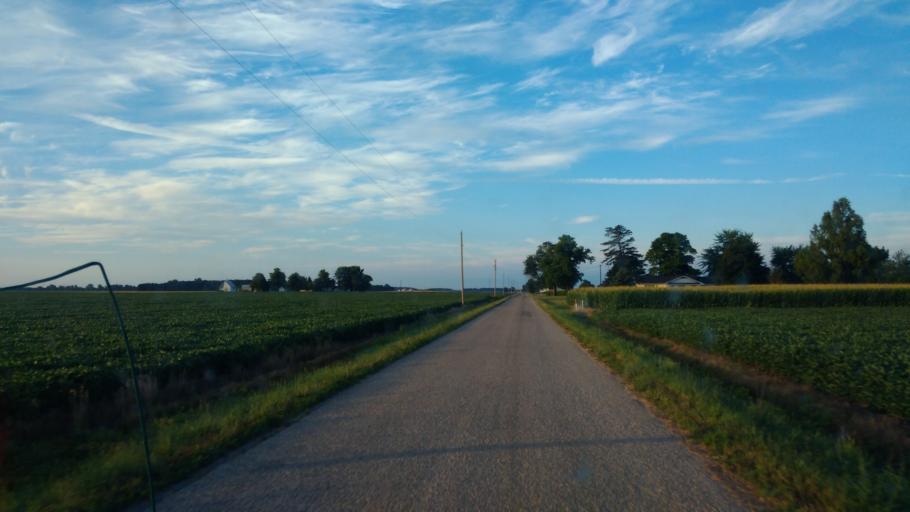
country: US
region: Indiana
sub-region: Adams County
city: Berne
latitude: 40.6527
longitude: -85.0608
